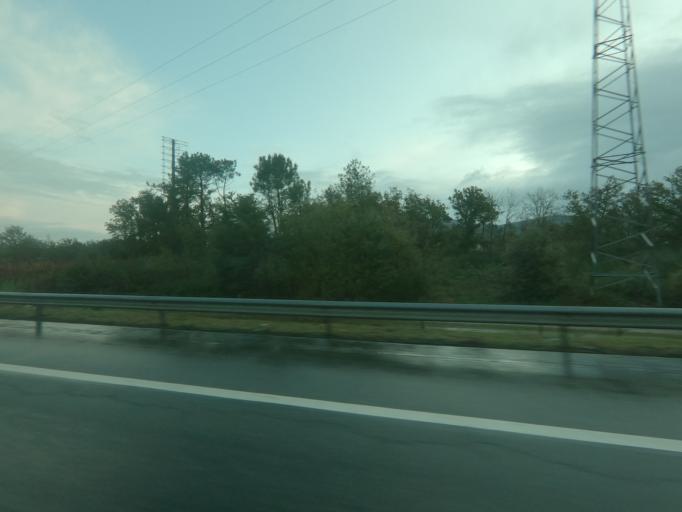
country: PT
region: Viana do Castelo
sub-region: Valenca
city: Valenza
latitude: 42.0026
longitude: -8.6449
